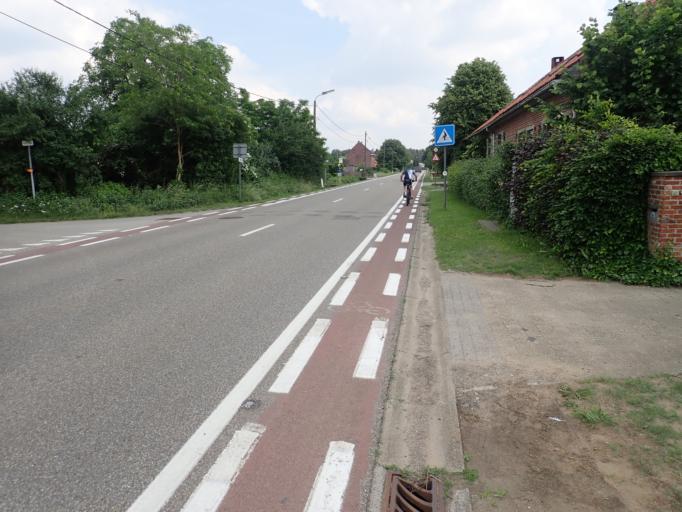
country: BE
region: Flanders
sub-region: Provincie Antwerpen
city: Lille
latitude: 51.2253
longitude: 4.8854
